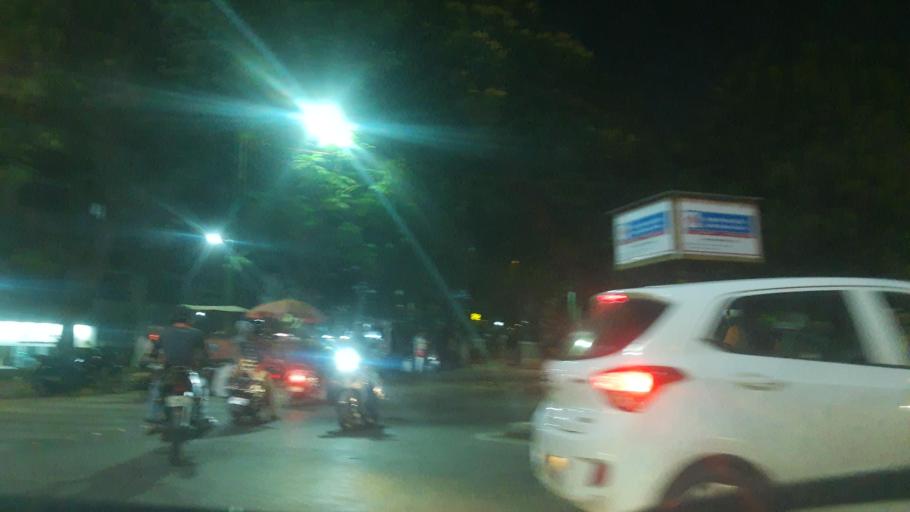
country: IN
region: Maharashtra
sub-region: Thane
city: Thane
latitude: 19.2044
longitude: 72.9690
